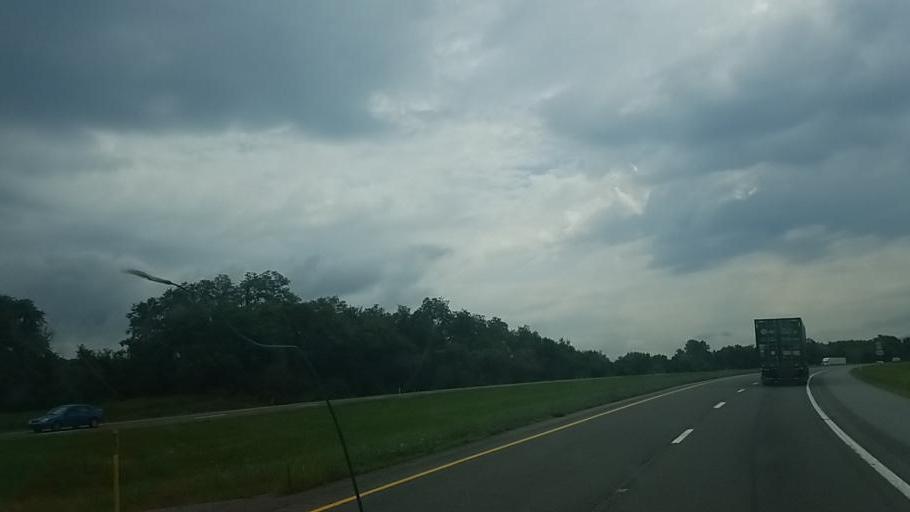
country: US
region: Pennsylvania
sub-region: Juniata County
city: Mifflintown
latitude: 40.6041
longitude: -77.4027
